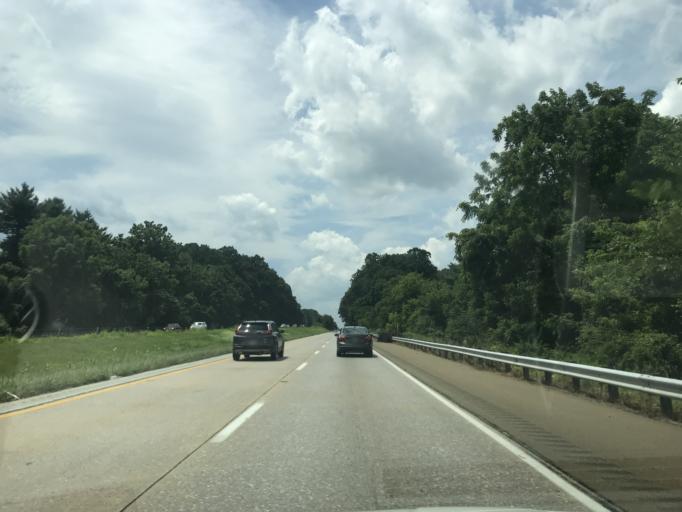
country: US
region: Pennsylvania
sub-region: Chester County
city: Kennett Square
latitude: 39.8534
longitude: -75.7320
